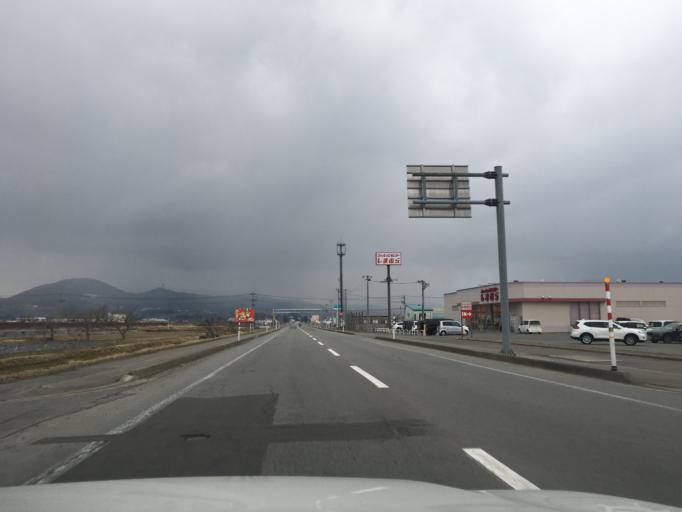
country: JP
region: Aomori
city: Kuroishi
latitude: 40.5814
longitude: 140.5686
